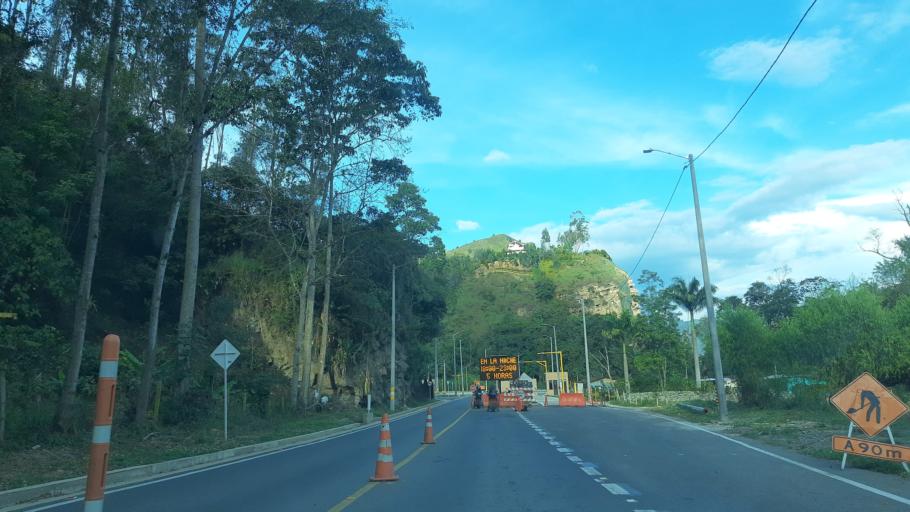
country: CO
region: Cundinamarca
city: Macheta
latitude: 5.0749
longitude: -73.5861
